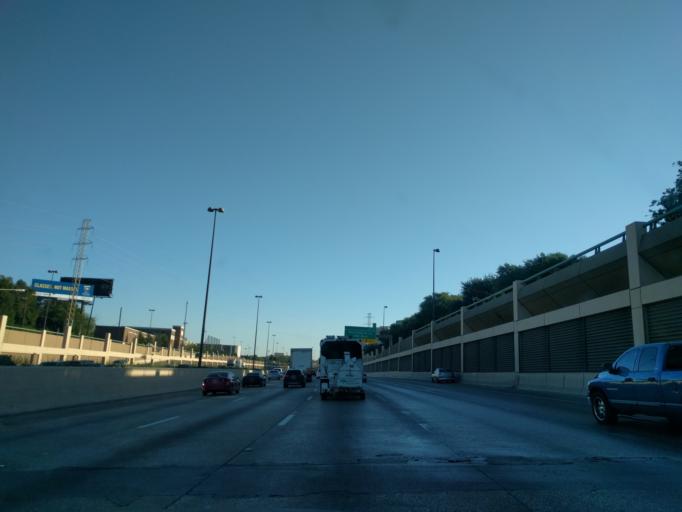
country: US
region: Texas
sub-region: Dallas County
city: Highland Park
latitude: 32.8315
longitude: -96.7807
